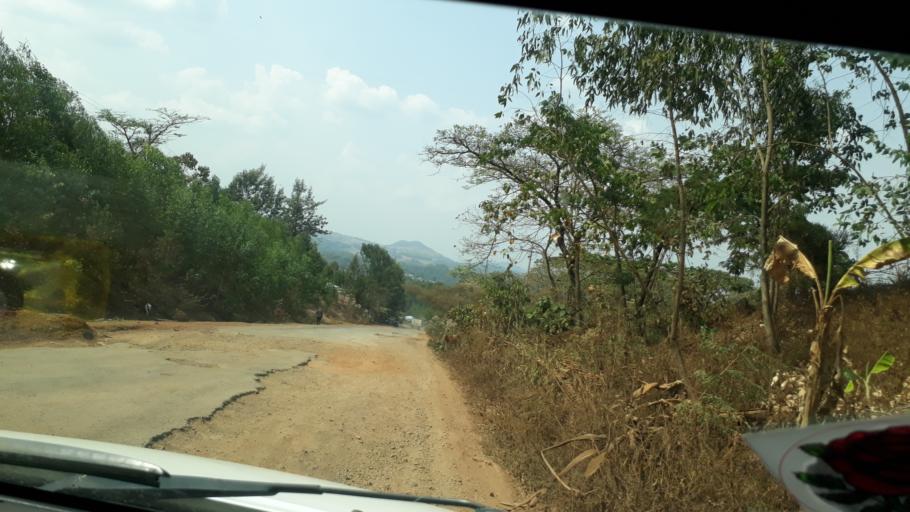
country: ET
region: Oromiya
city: Agaro
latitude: 7.9356
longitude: 36.5128
